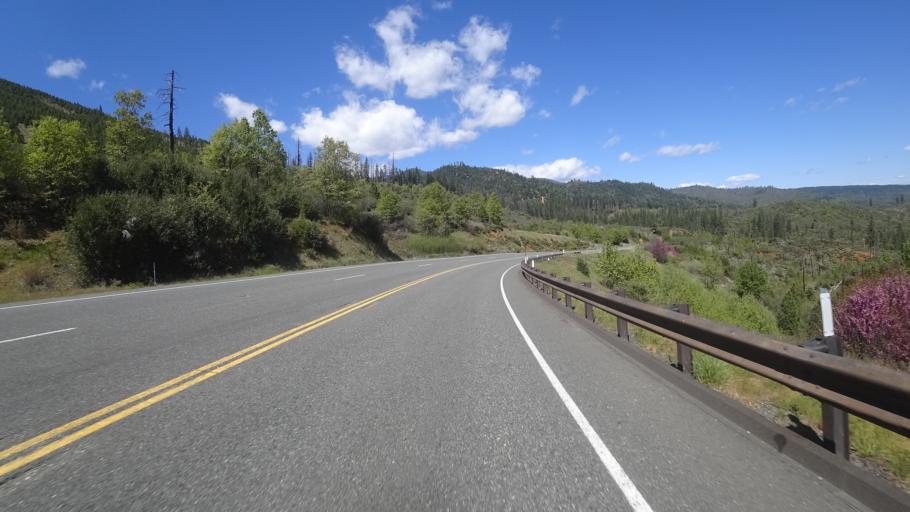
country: US
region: California
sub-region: Trinity County
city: Weaverville
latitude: 40.7436
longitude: -122.9763
